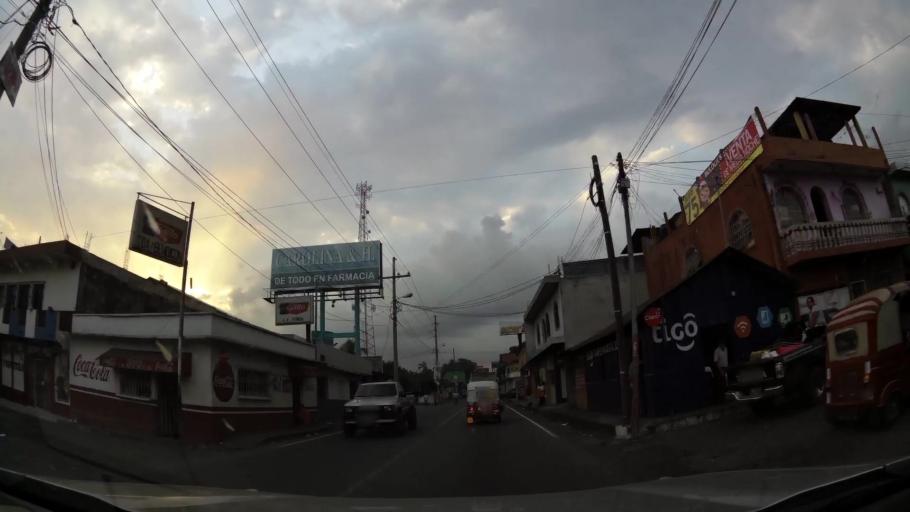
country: GT
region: Escuintla
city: Siquinala
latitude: 14.3065
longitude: -90.9655
